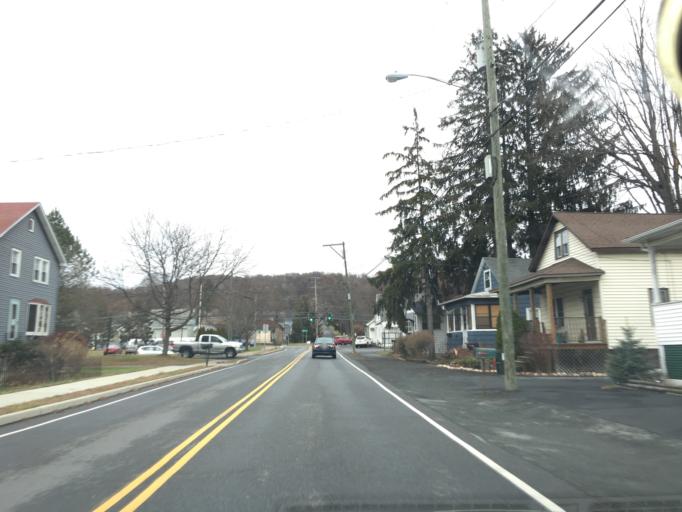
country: US
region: New York
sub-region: Rensselaer County
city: Wynantskill
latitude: 42.6958
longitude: -73.6450
